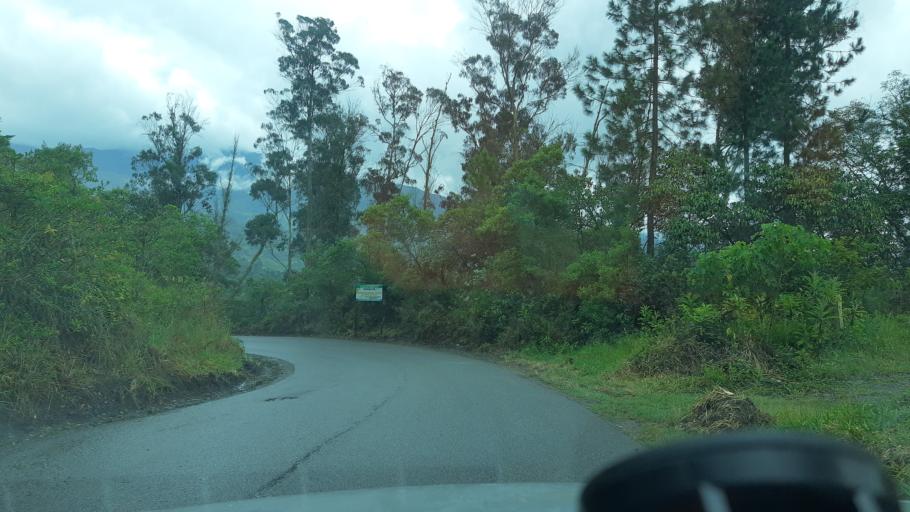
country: CO
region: Boyaca
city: Chinavita
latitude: 5.1539
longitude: -73.3692
